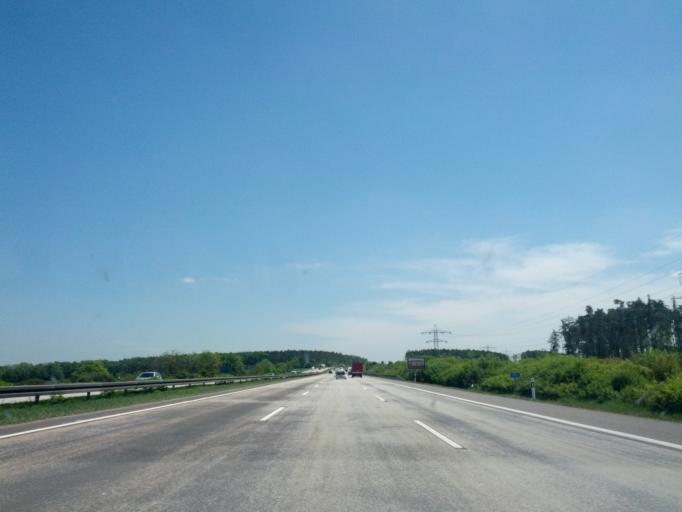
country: DE
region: Thuringia
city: Troistedt
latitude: 50.9481
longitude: 11.2660
